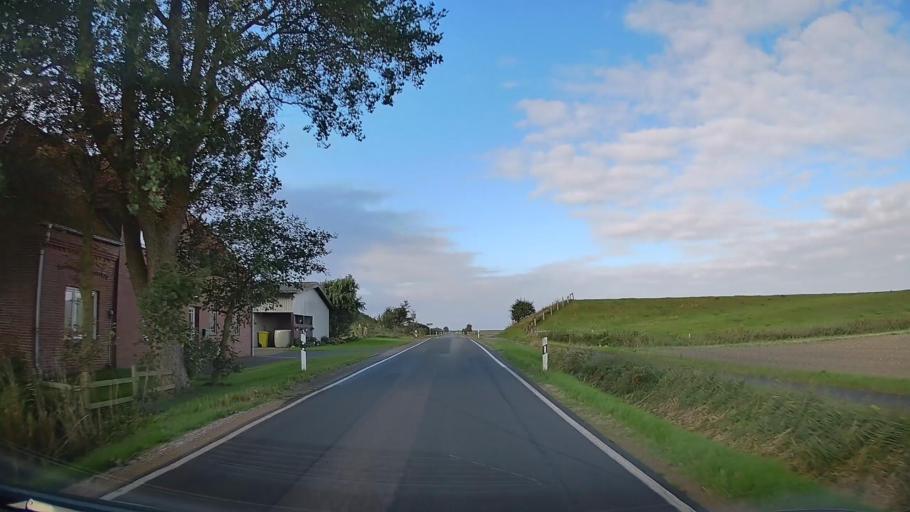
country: DE
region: Schleswig-Holstein
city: Reussenkoge
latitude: 54.5715
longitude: 8.9399
